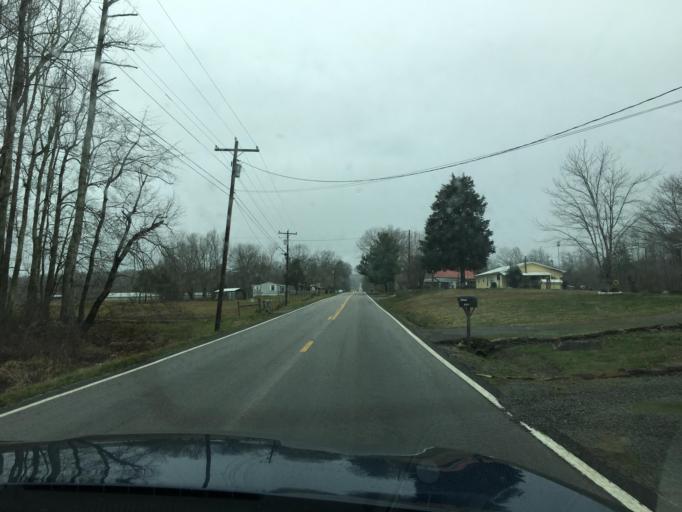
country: US
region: Tennessee
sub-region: Rhea County
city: Spring City
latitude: 35.7547
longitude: -84.8527
